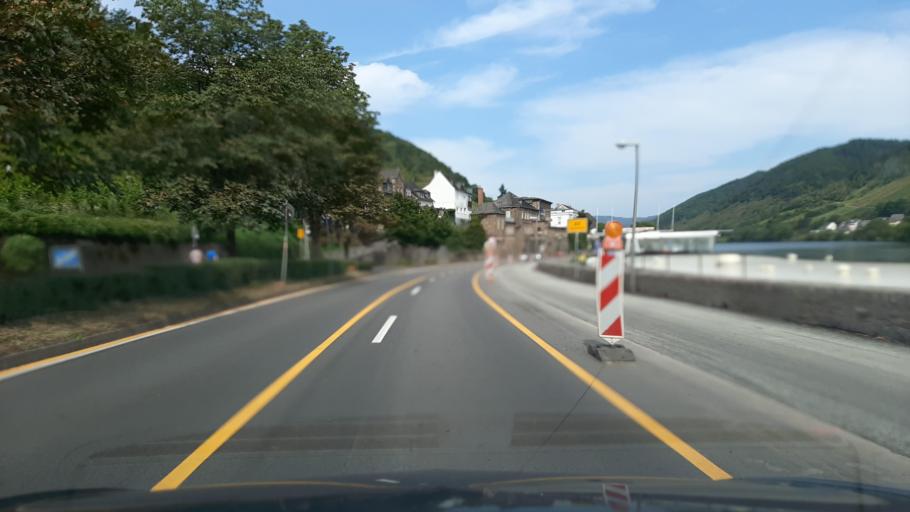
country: DE
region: Rheinland-Pfalz
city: Alf
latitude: 50.0535
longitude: 7.1273
